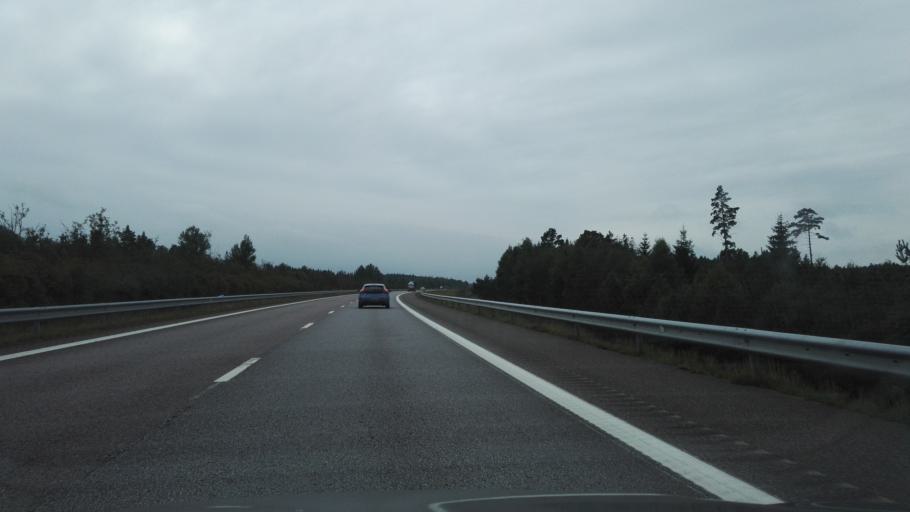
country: SE
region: Kronoberg
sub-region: Markaryds Kommun
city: Stromsnasbruk
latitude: 56.6820
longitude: 13.8326
